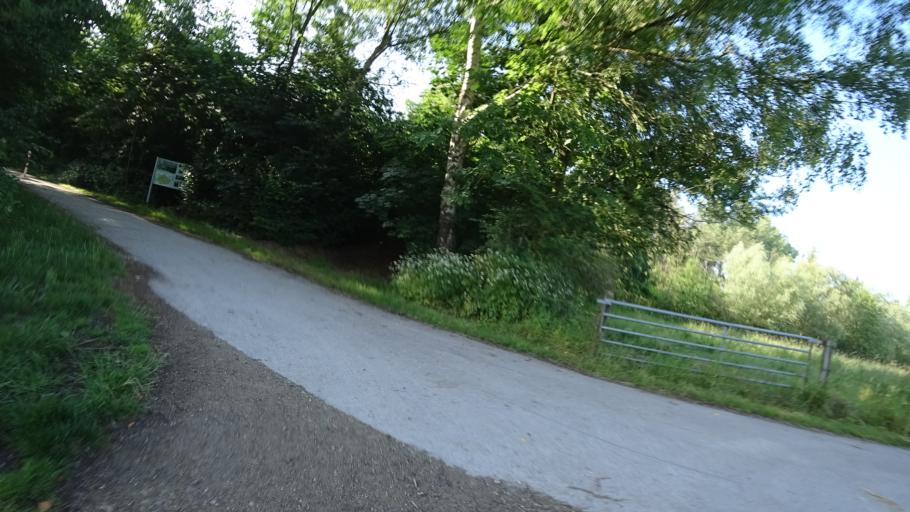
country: DE
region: North Rhine-Westphalia
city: Erwitte
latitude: 51.6369
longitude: 8.3765
